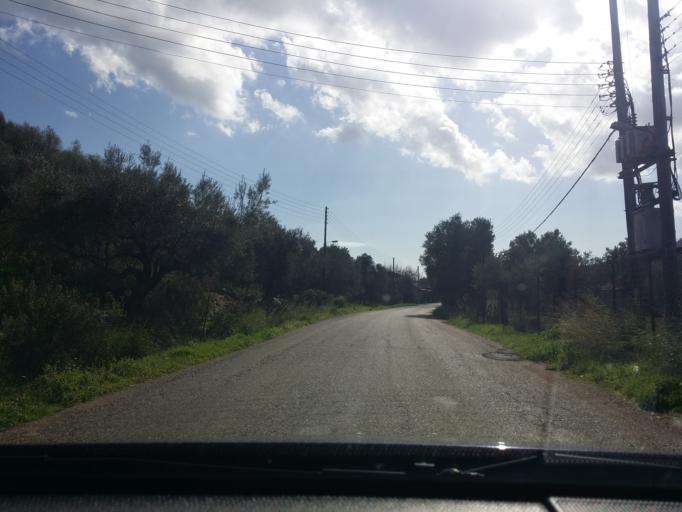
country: GR
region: West Greece
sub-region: Nomos Aitolias kai Akarnanias
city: Astakos
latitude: 38.5882
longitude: 21.0897
